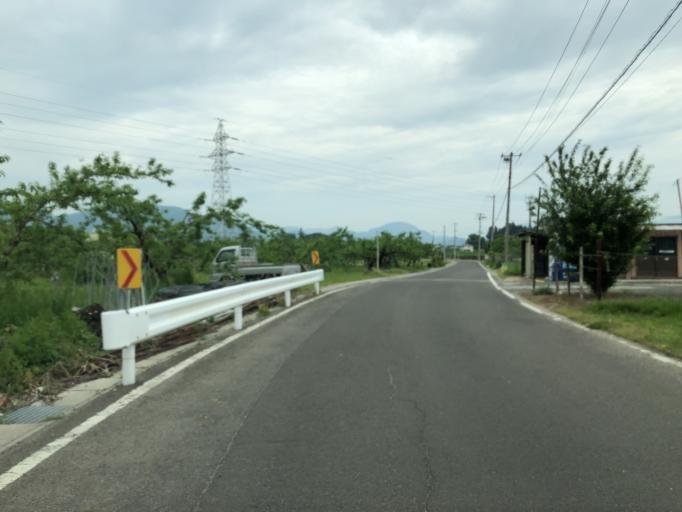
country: JP
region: Fukushima
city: Fukushima-shi
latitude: 37.7844
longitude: 140.4213
